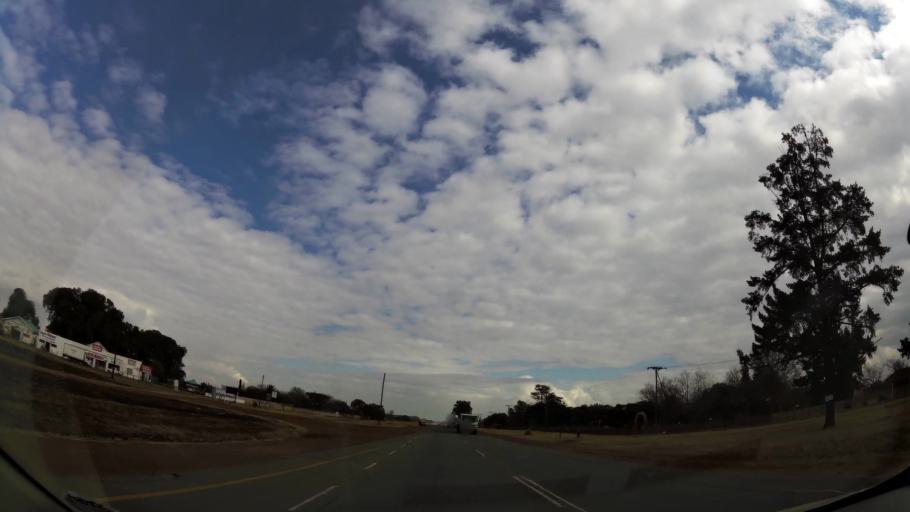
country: ZA
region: Gauteng
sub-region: Sedibeng District Municipality
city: Meyerton
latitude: -26.6363
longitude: 28.0580
